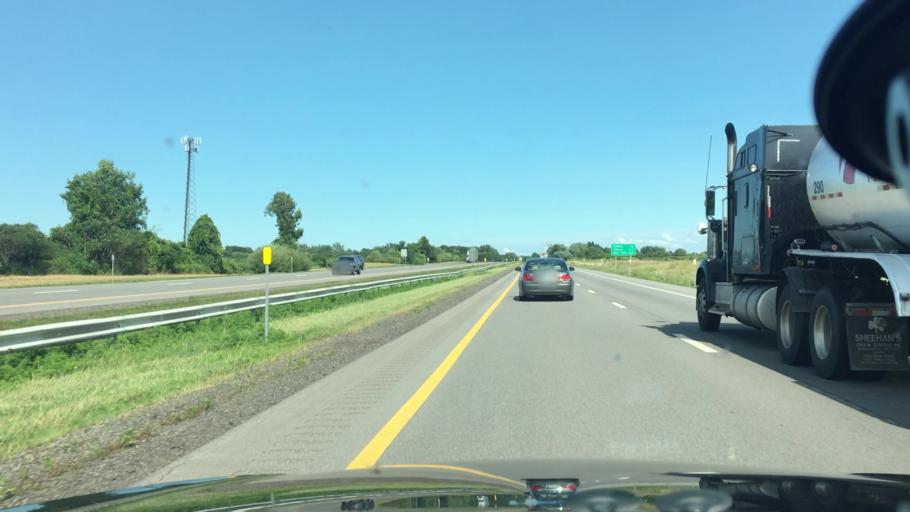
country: US
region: New York
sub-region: Chautauqua County
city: Silver Creek
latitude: 42.5124
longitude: -79.1825
